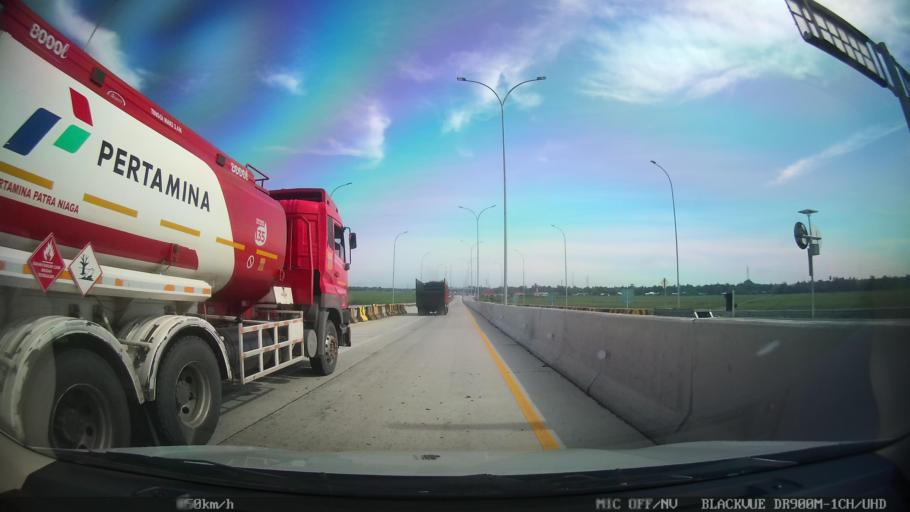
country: ID
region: North Sumatra
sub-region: Kabupaten Langkat
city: Stabat
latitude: 3.7149
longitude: 98.4938
